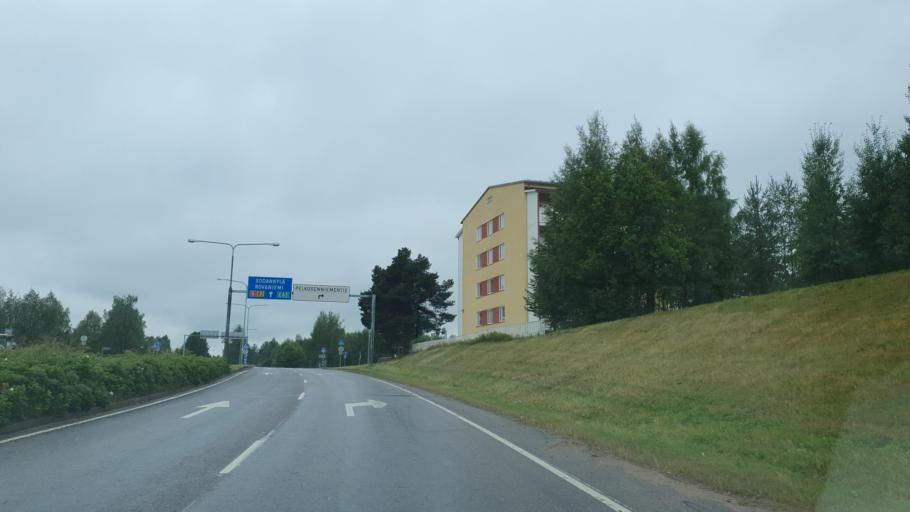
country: FI
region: Lapland
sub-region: Itae-Lappi
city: Kemijaervi
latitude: 66.7211
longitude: 27.3993
